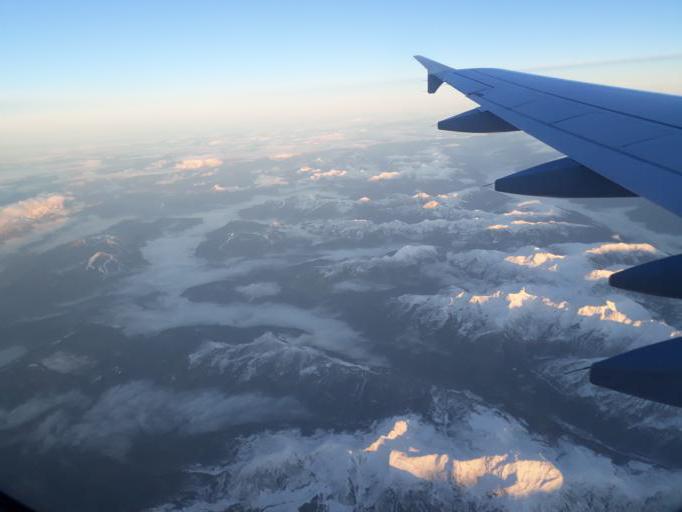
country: AT
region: Tyrol
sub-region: Politischer Bezirk Schwaz
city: Stummerberg
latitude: 47.3329
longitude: 11.9200
